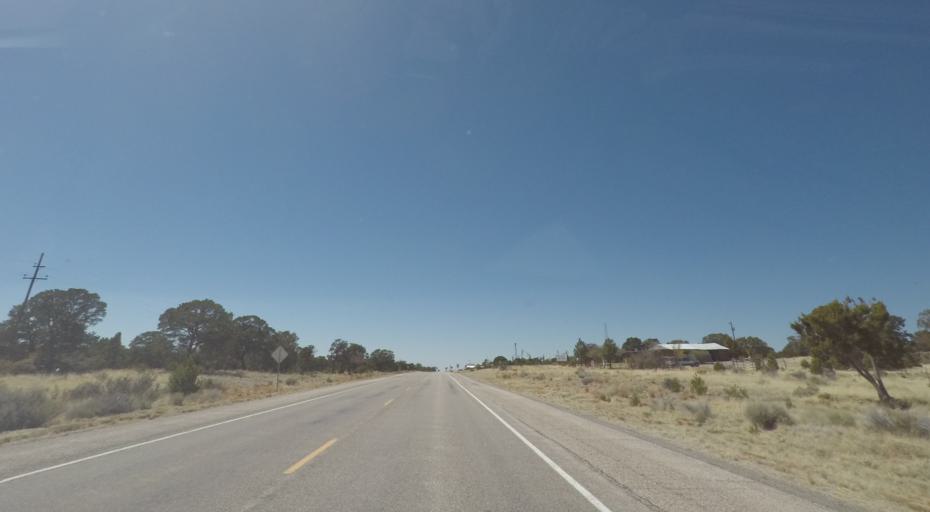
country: US
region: New Mexico
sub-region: Socorro County
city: Alamo
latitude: 34.2972
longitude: -108.1243
